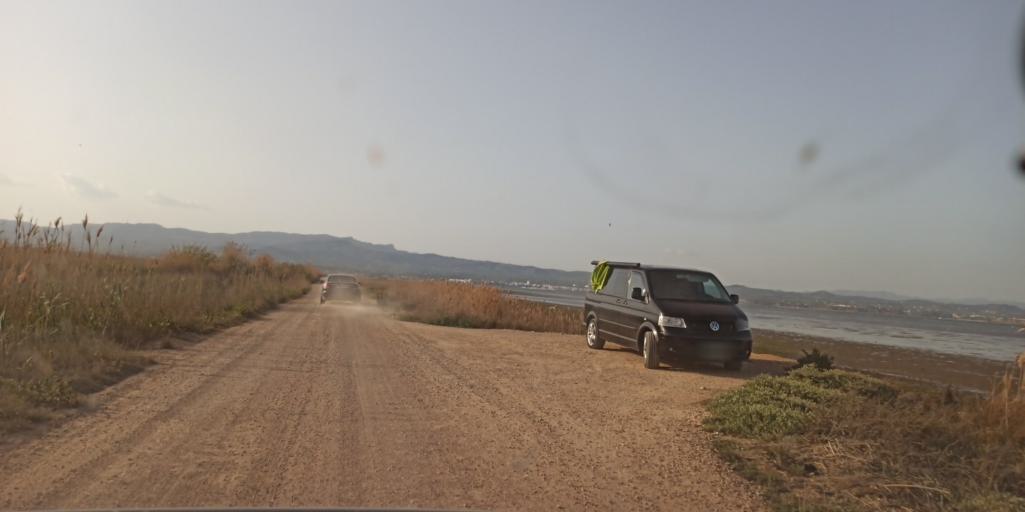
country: ES
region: Catalonia
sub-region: Provincia de Tarragona
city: L'Ampolla
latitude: 40.7737
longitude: 0.7260
